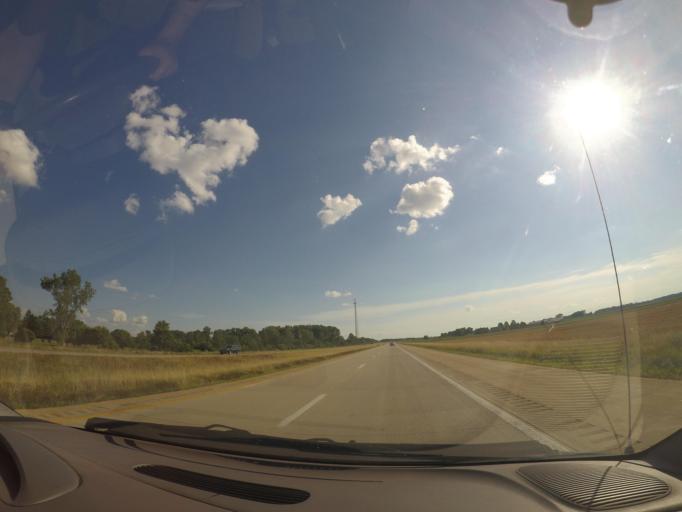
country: US
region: Ohio
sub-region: Lucas County
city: Whitehouse
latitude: 41.4662
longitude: -83.7817
